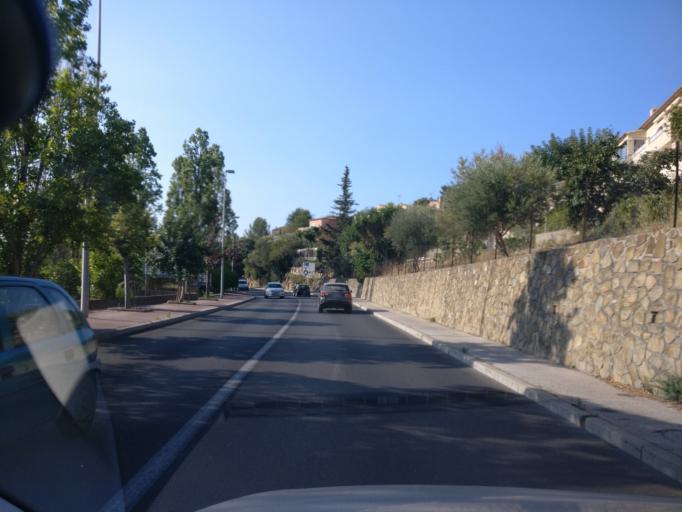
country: FR
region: Provence-Alpes-Cote d'Azur
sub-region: Departement du Var
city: Ollioules
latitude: 43.1311
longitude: 5.8443
